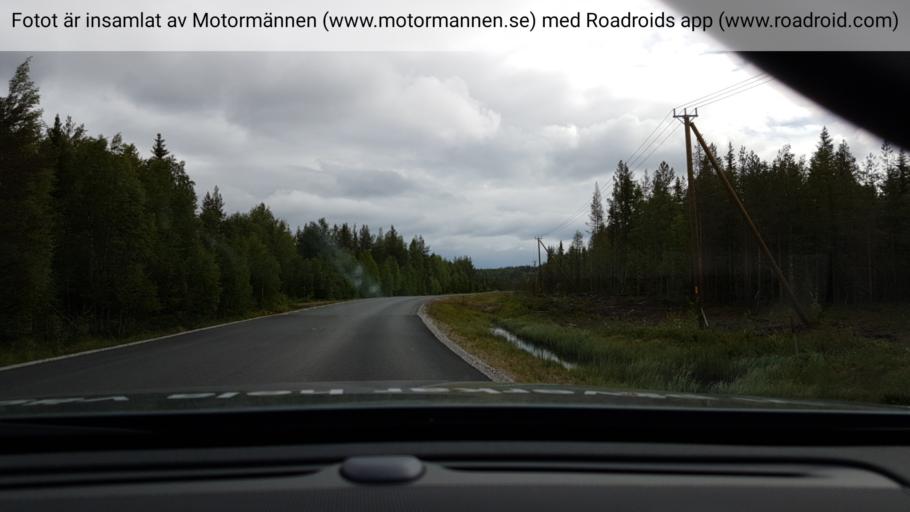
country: SE
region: Vaesterbotten
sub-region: Asele Kommun
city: Insjon
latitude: 64.2755
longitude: 17.5882
